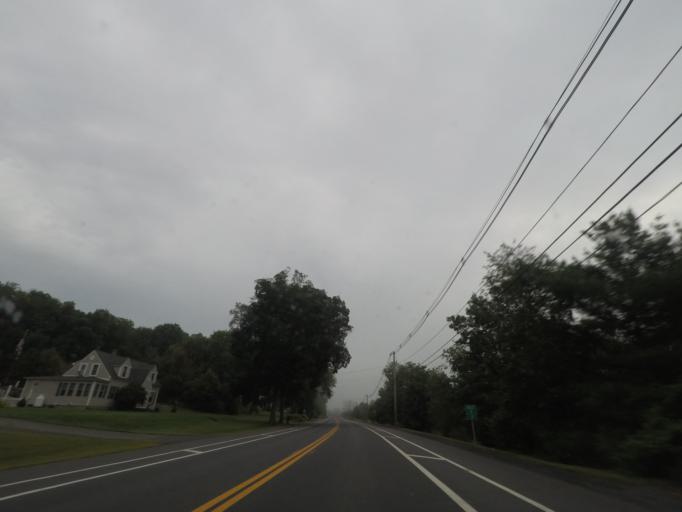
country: US
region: Massachusetts
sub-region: Hampden County
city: Palmer
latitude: 42.1446
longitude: -72.2793
